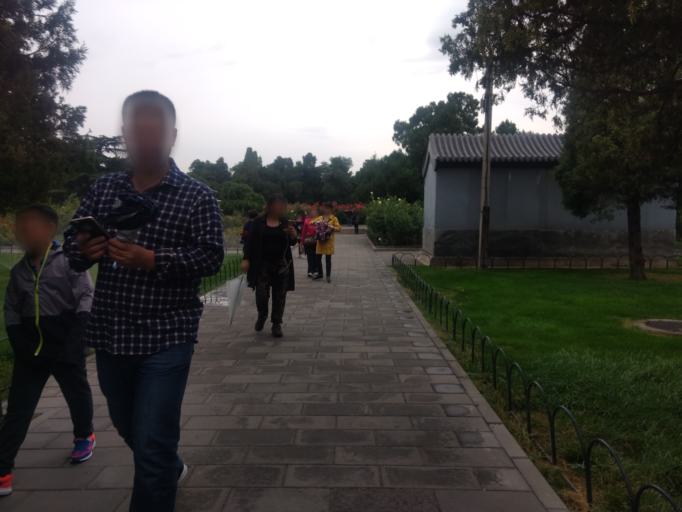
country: CN
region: Beijing
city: Longtan
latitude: 39.8809
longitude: 116.4027
